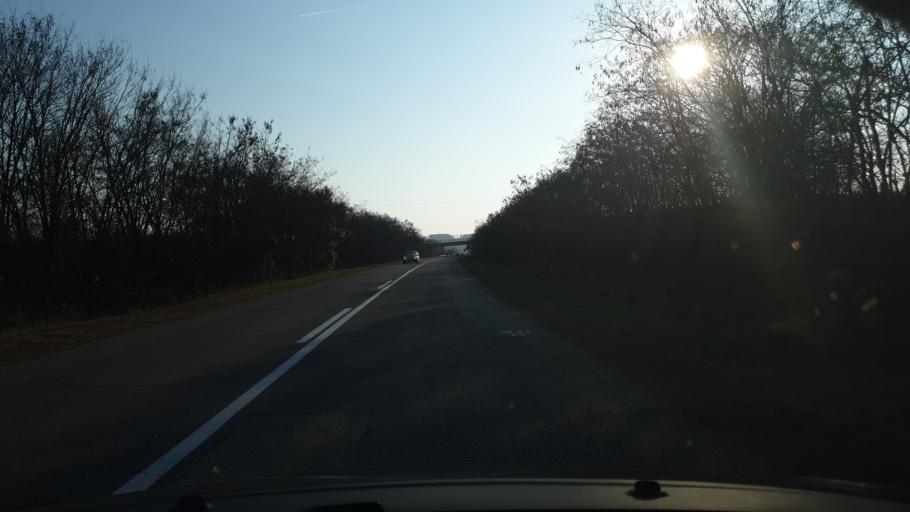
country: RS
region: Central Serbia
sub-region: Zajecarski Okrug
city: Zajecar
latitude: 44.0929
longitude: 22.3454
